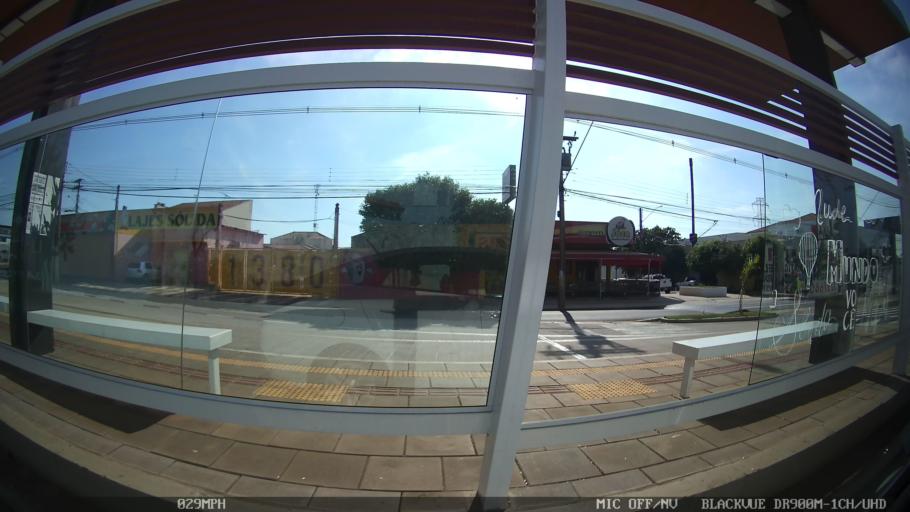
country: BR
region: Sao Paulo
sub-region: Sao Jose Do Rio Preto
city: Sao Jose do Rio Preto
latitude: -20.7935
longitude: -49.4161
